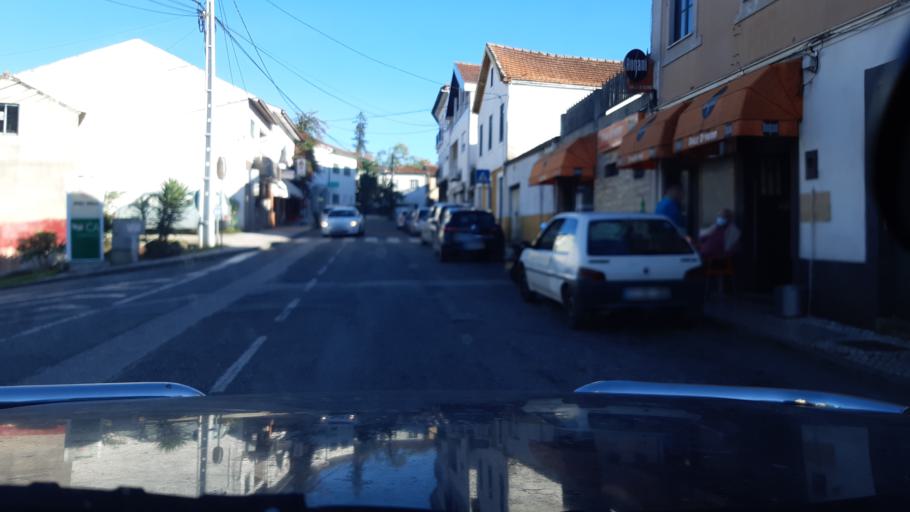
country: PT
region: Aveiro
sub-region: Agueda
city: Agueda
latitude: 40.5610
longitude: -8.4424
